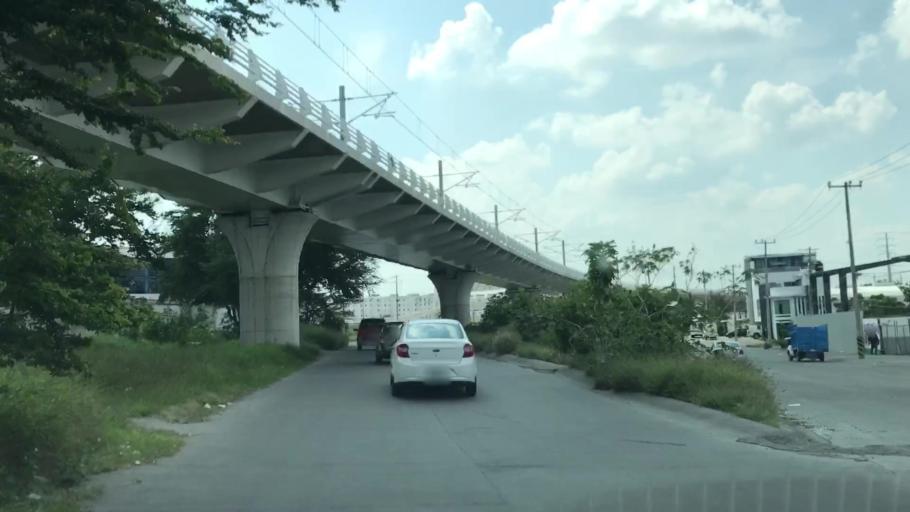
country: MX
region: Jalisco
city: Tlaquepaque
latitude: 20.6247
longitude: -103.2891
